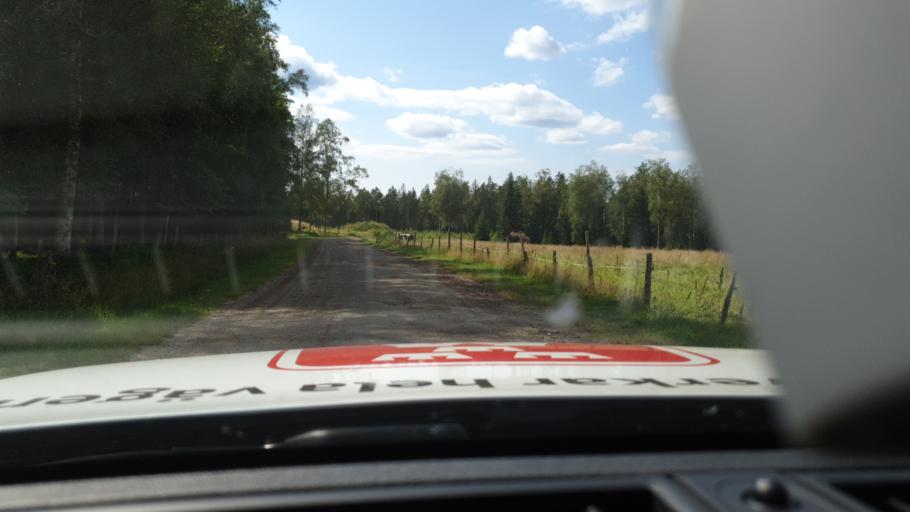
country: SE
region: Joenkoeping
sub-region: Gnosjo Kommun
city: Marieholm
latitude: 57.5611
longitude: 13.9101
